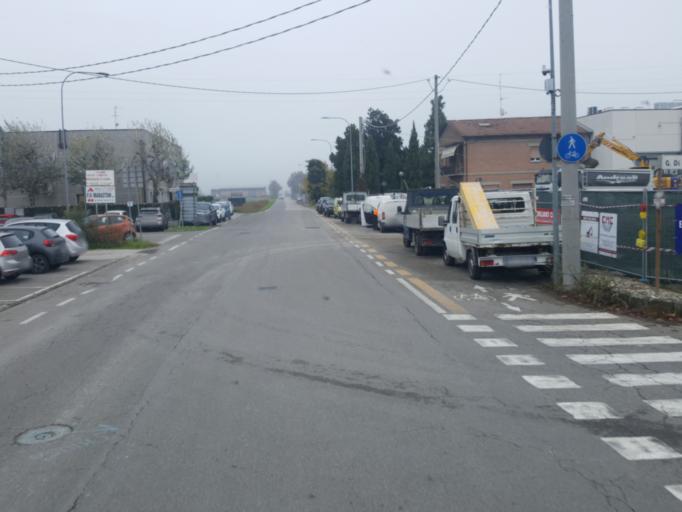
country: IT
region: Emilia-Romagna
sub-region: Provincia di Reggio Emilia
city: Codemondo-Quaresimo
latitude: 44.7197
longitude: 10.5529
